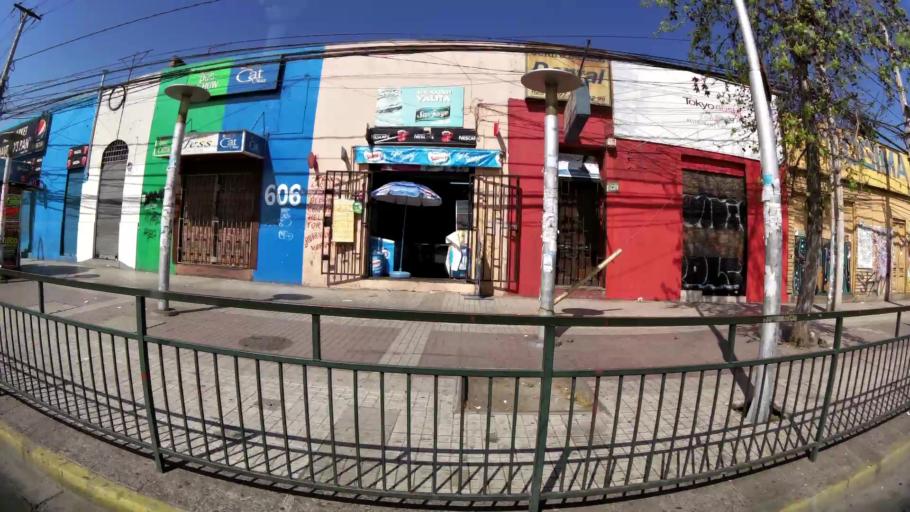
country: CL
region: Santiago Metropolitan
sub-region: Provincia de Santiago
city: Santiago
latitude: -33.4061
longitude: -70.6435
